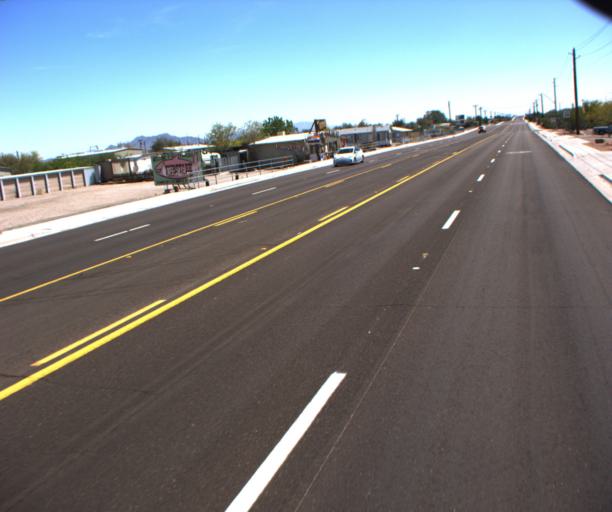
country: US
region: Arizona
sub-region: La Paz County
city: Quartzsite
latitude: 33.6782
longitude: -114.2172
